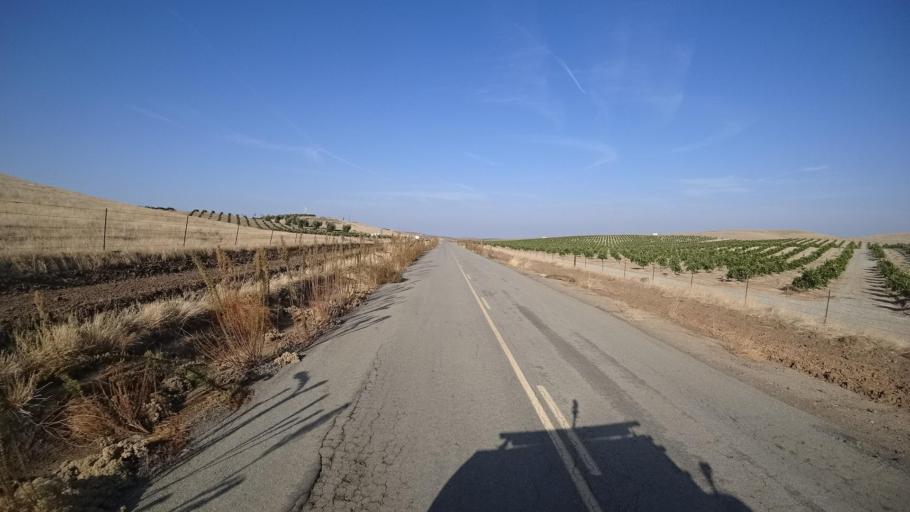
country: US
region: California
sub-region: Tulare County
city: Richgrove
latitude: 35.6427
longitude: -119.0489
